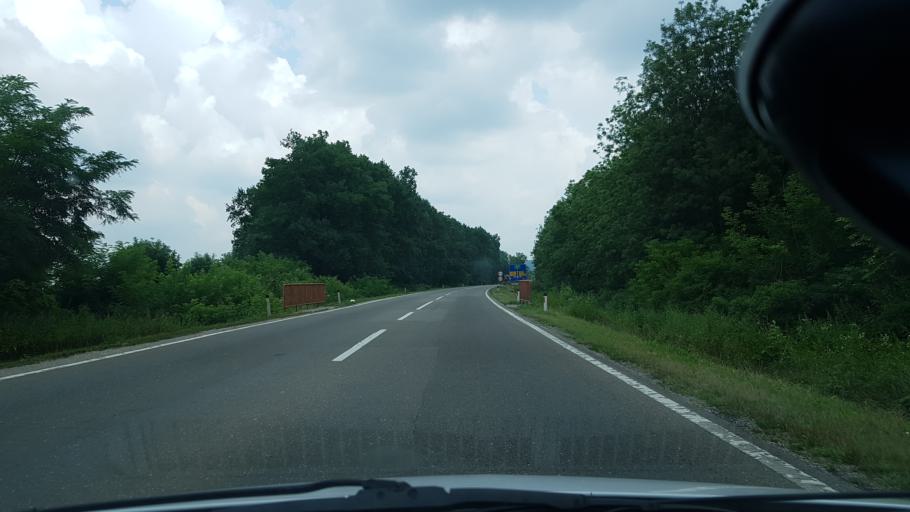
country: RS
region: Central Serbia
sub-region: Sumadijski Okrug
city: Batocina
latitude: 44.1468
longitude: 21.1020
